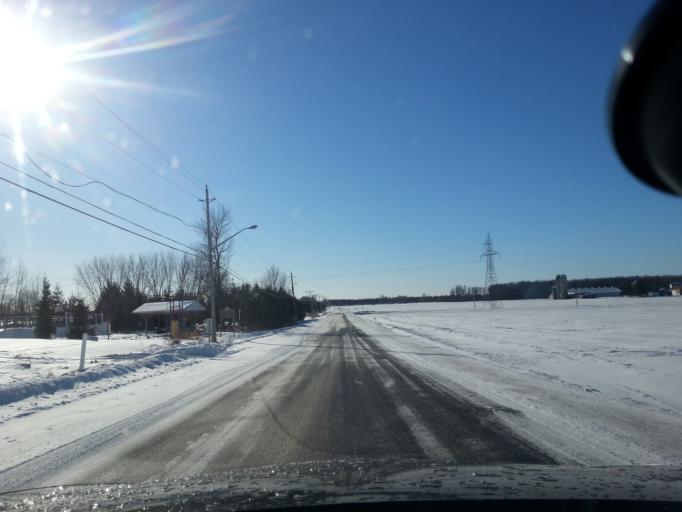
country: CA
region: Ontario
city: Clarence-Rockland
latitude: 45.2997
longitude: -75.3979
